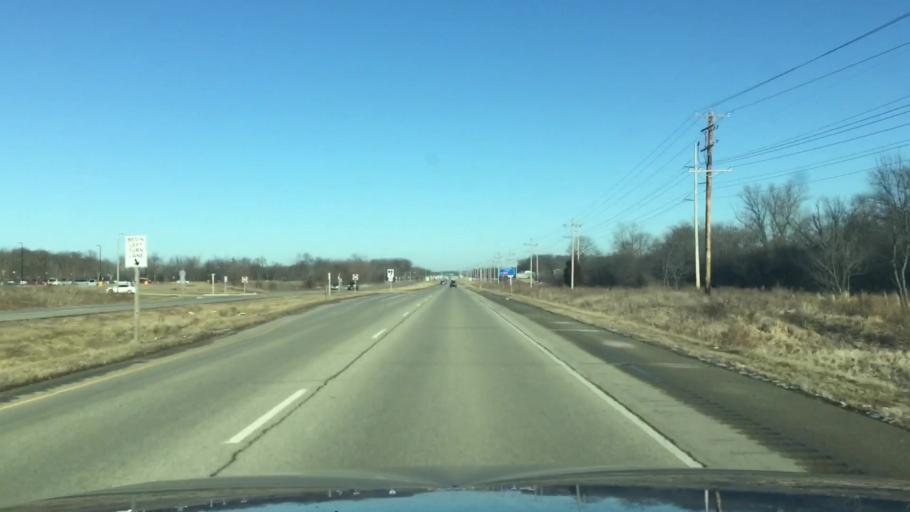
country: US
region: Wisconsin
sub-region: Racine County
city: Browns Lake
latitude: 42.7003
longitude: -88.2551
